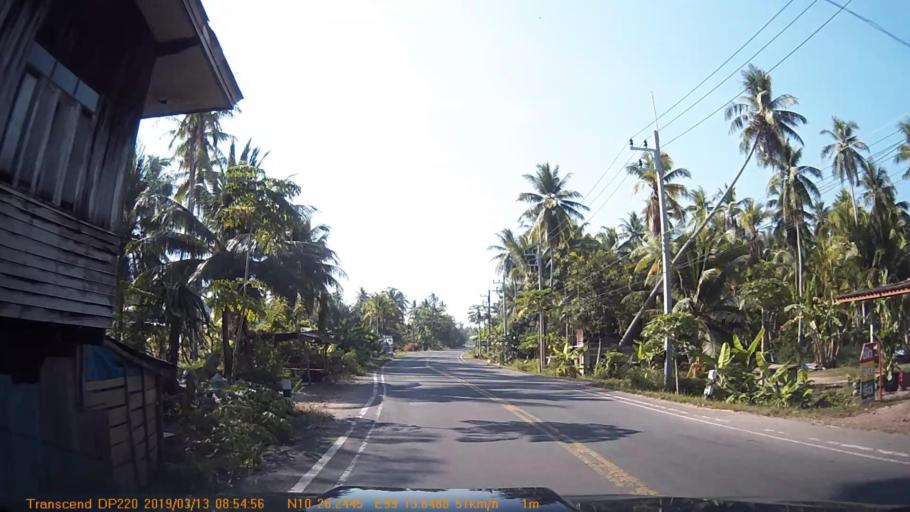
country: TH
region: Chumphon
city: Chumphon
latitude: 10.4706
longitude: 99.2275
